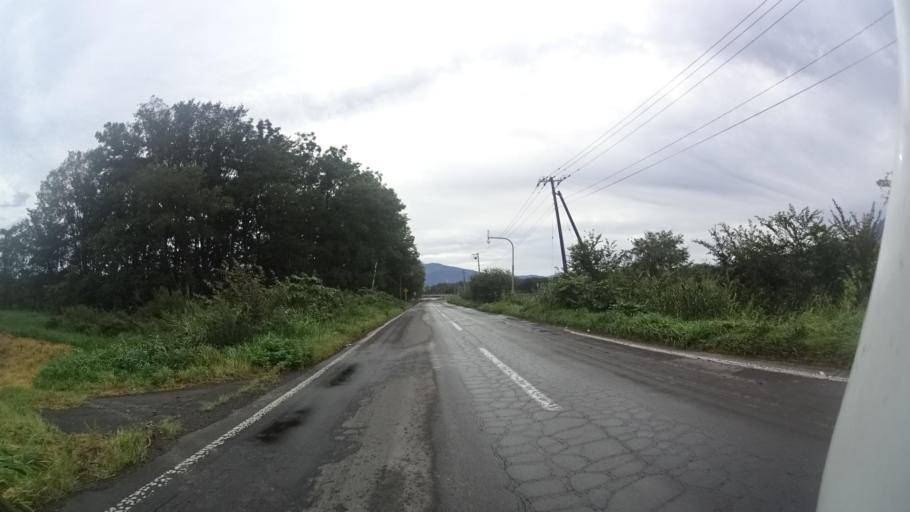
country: JP
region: Hokkaido
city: Abashiri
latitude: 43.8714
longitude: 144.6790
